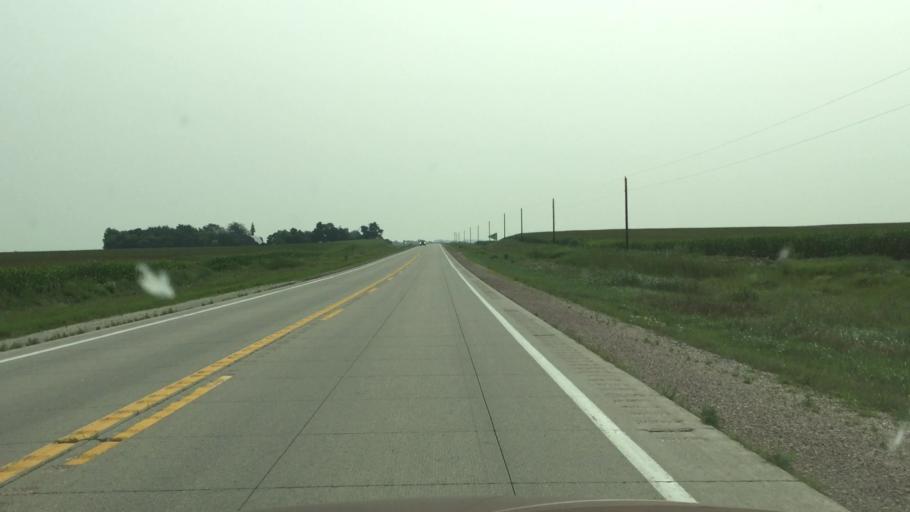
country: US
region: Iowa
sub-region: Osceola County
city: Sibley
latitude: 43.4328
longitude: -95.6317
